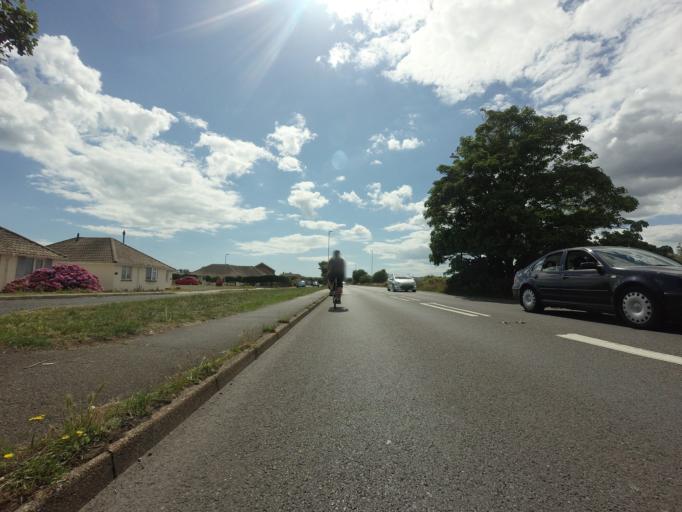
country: GB
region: England
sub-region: East Sussex
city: Pevensey
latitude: 50.8096
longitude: 0.3442
